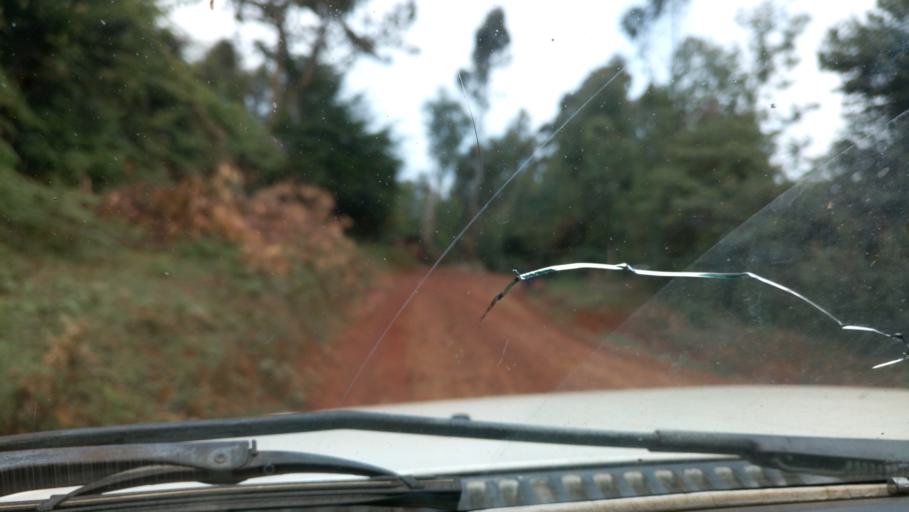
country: KE
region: Nyeri
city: Othaya
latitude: -0.5882
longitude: 36.9921
